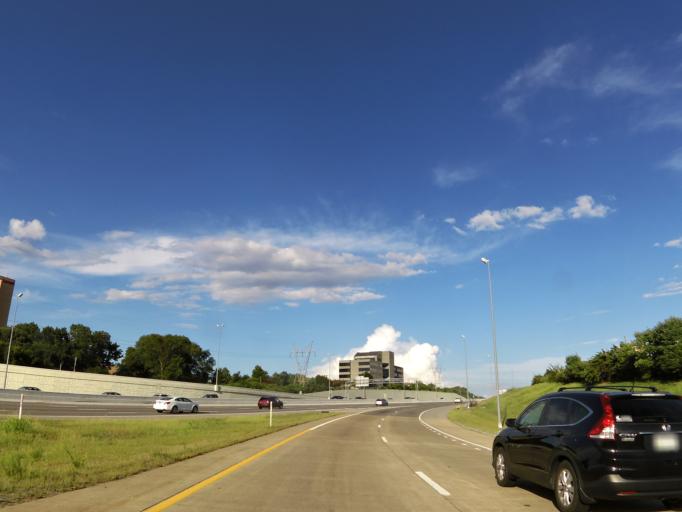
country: US
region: Tennessee
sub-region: Davidson County
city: Nashville
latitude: 36.1439
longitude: -86.6946
